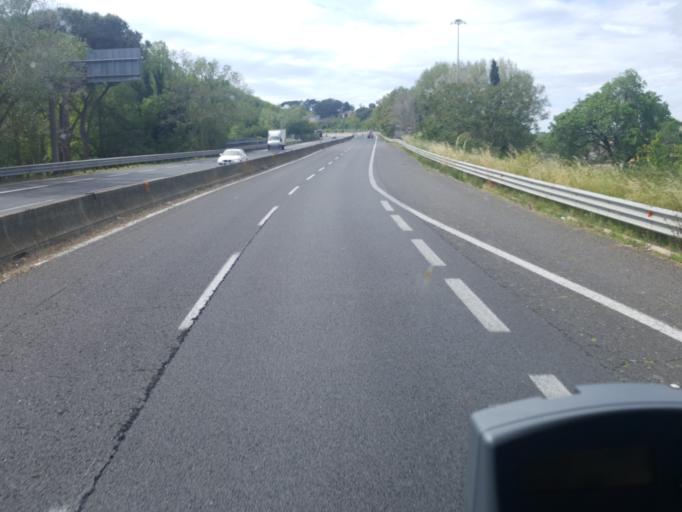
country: IT
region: Latium
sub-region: Citta metropolitana di Roma Capitale
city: Ara Nova
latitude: 41.9075
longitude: 12.2635
